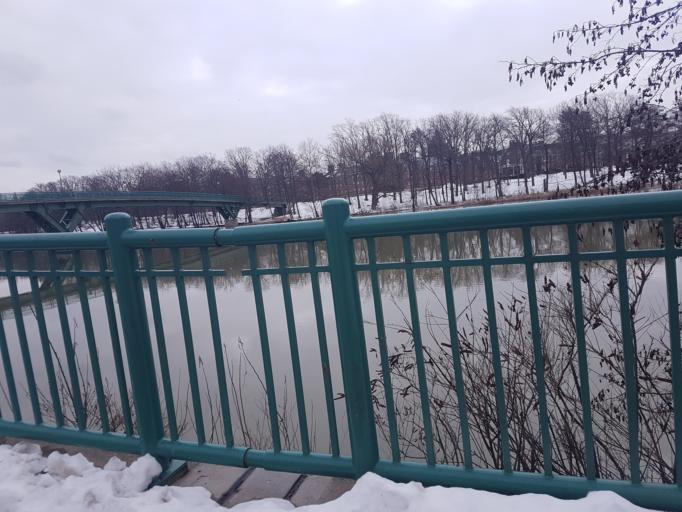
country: US
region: New York
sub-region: Monroe County
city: Rochester
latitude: 43.1312
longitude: -77.6346
